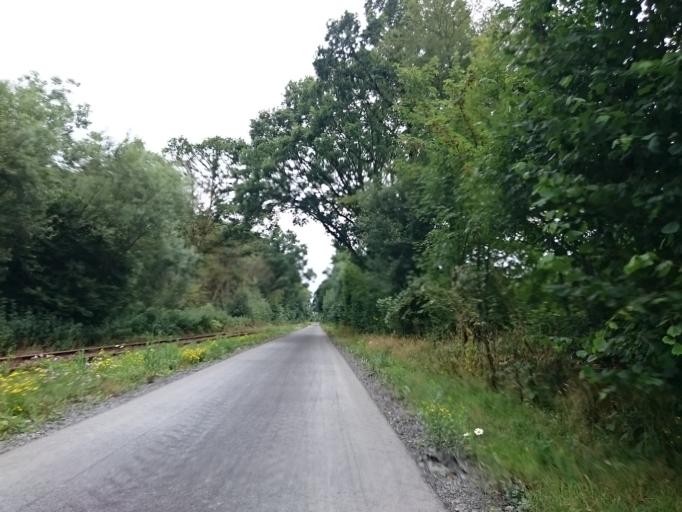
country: FR
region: Lower Normandy
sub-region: Departement du Calvados
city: Sainte-Honorine-du-Fay
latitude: 49.0403
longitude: -0.4638
